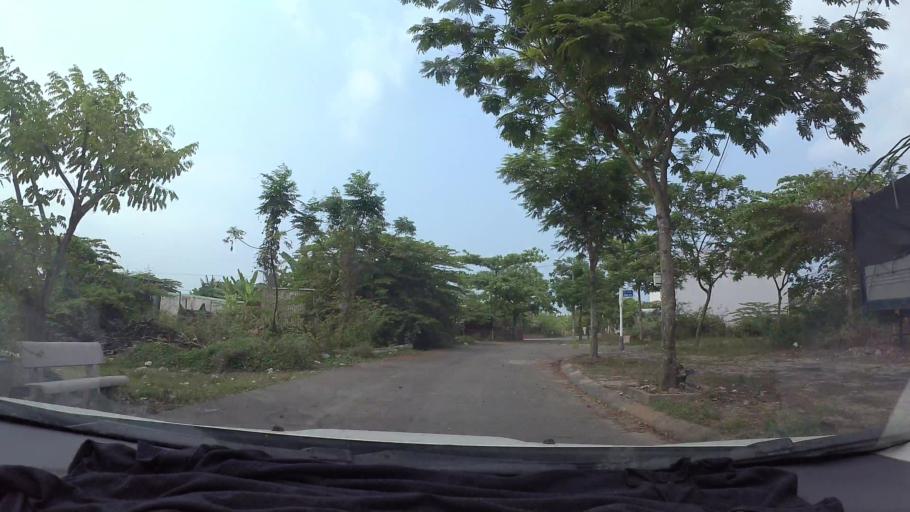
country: VN
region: Da Nang
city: Lien Chieu
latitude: 16.0579
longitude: 108.1591
